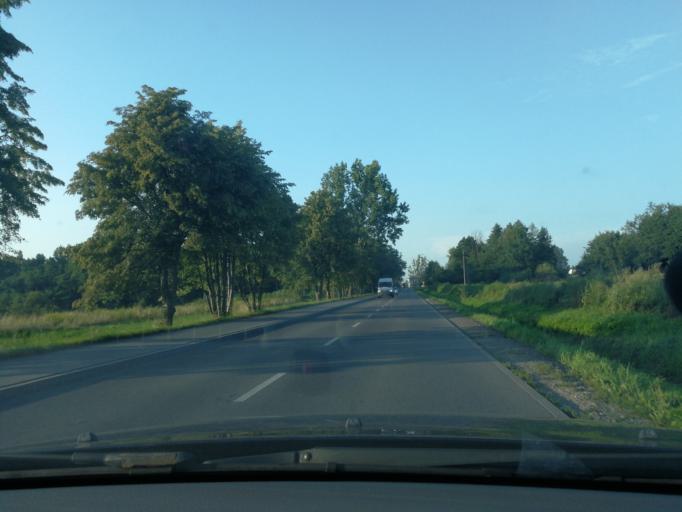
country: PL
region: Masovian Voivodeship
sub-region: Powiat warszawski zachodni
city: Ozarow Mazowiecki
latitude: 52.1866
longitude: 20.7516
